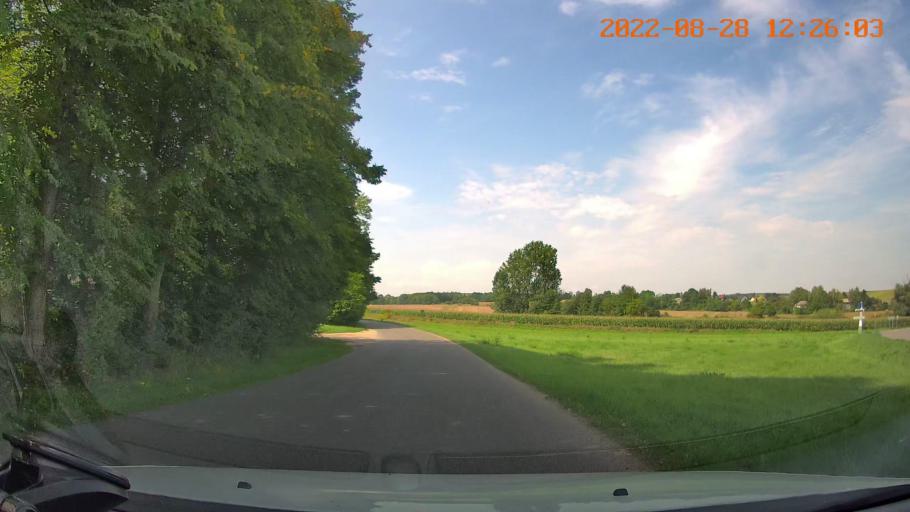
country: PL
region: Swietokrzyskie
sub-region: Powiat pinczowski
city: Michalow
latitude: 50.4385
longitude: 20.4991
